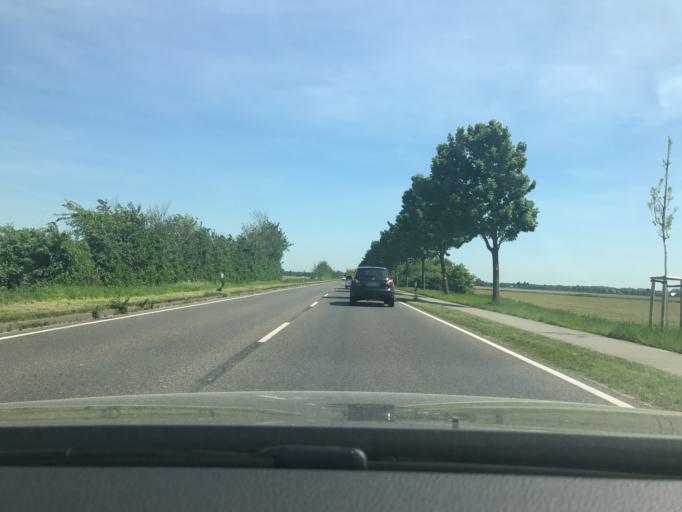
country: DE
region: North Rhine-Westphalia
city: Tonisvorst
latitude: 51.2818
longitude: 6.4838
